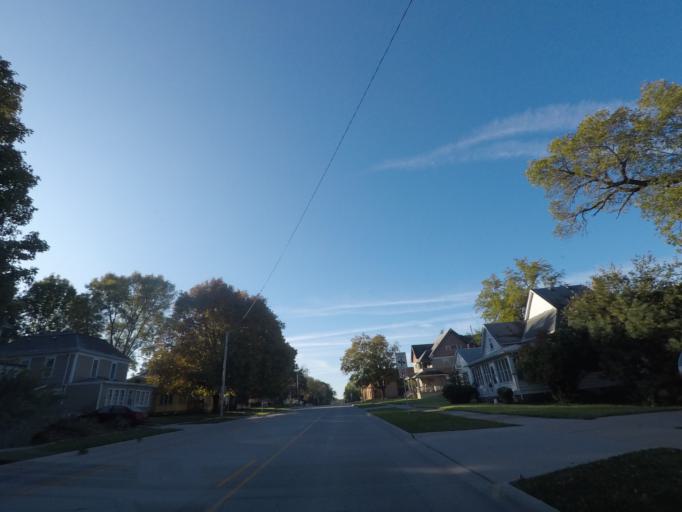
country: US
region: Iowa
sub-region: Story County
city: Nevada
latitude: 42.0184
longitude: -93.4523
